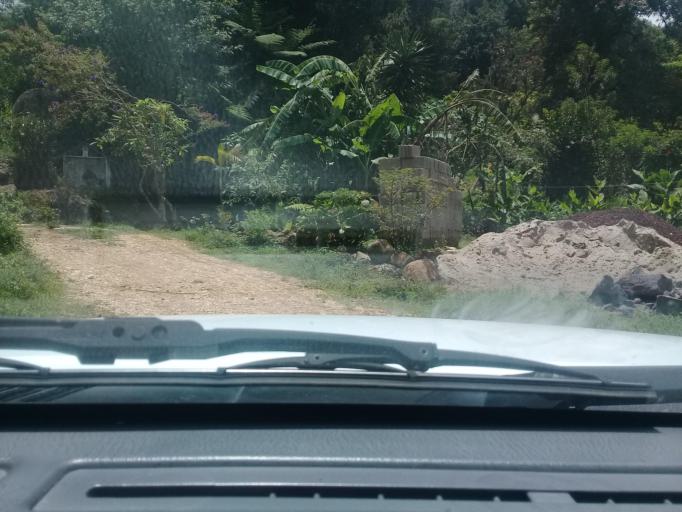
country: MX
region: Veracruz
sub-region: Tlalnelhuayocan
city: Otilpan
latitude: 19.5431
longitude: -96.9774
